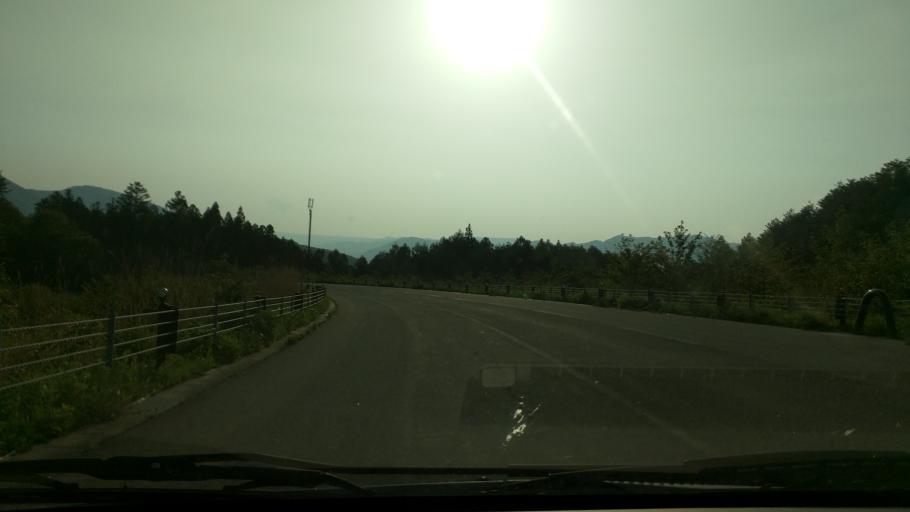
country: JP
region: Tochigi
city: Kuroiso
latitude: 37.2081
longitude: 139.9144
